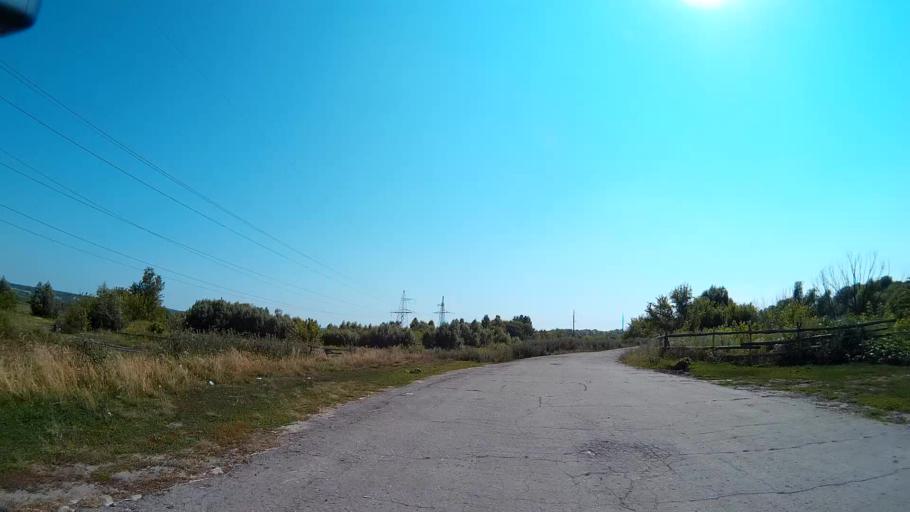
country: RU
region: Ulyanovsk
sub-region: Ulyanovskiy Rayon
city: Ulyanovsk
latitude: 54.2384
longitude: 48.2664
